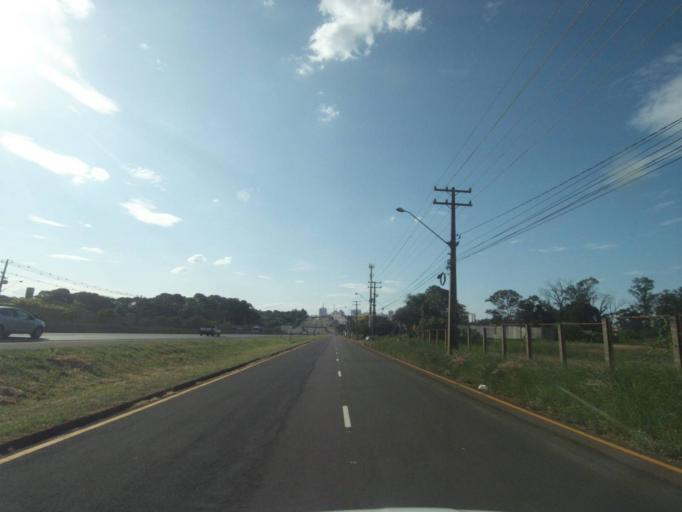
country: BR
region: Parana
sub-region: Londrina
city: Londrina
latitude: -23.3567
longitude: -51.1579
